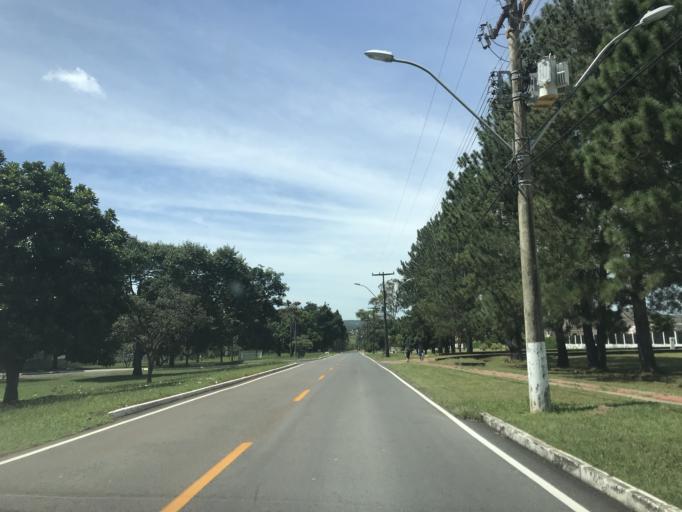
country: BR
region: Federal District
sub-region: Brasilia
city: Brasilia
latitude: -15.9092
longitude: -47.9347
